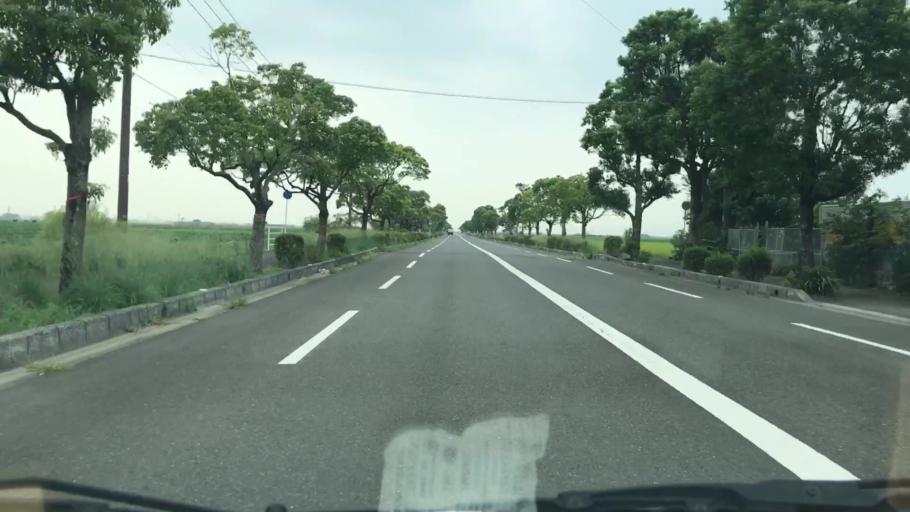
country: JP
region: Saga Prefecture
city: Okawa
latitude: 33.1909
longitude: 130.3029
